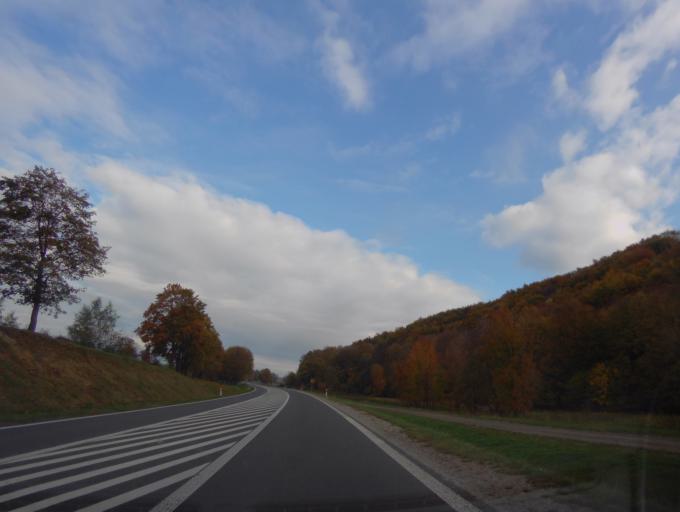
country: PL
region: Lublin Voivodeship
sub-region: Powiat bilgorajski
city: Goraj
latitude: 50.7558
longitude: 22.6720
